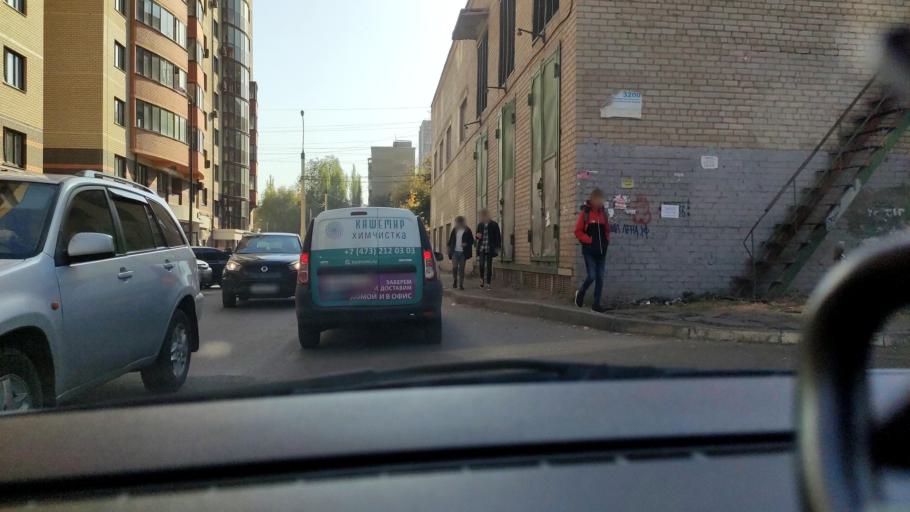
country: RU
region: Voronezj
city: Voronezh
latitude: 51.7040
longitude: 39.1868
